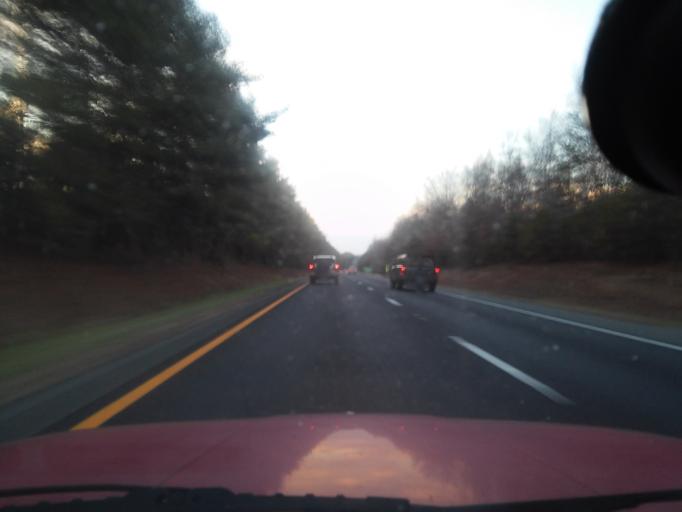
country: US
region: Virginia
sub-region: Fluvanna County
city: Palmyra
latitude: 37.9694
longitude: -78.1951
